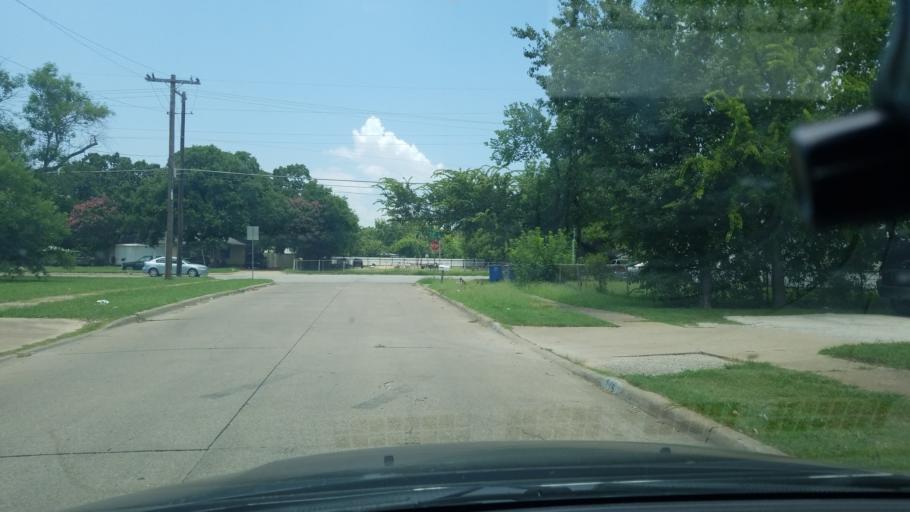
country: US
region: Texas
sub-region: Dallas County
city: Balch Springs
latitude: 32.7190
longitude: -96.6595
